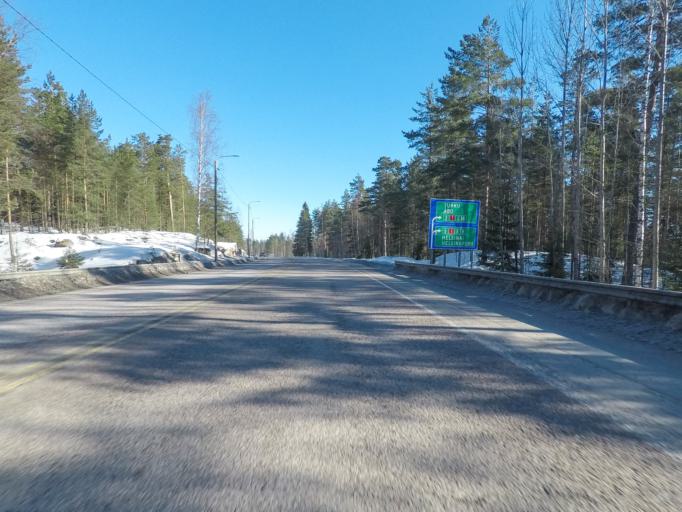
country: FI
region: Uusimaa
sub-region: Helsinki
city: Kirkkonummi
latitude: 60.2709
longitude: 24.4498
